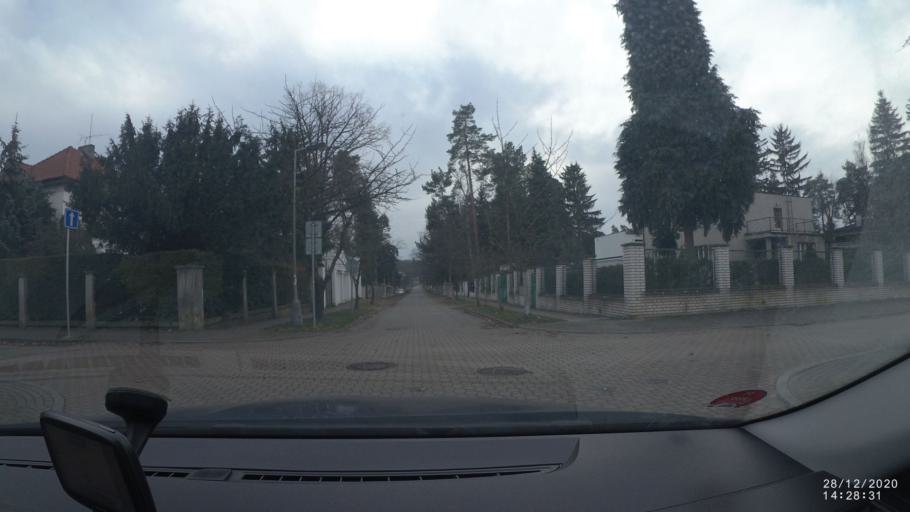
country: CZ
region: Central Bohemia
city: Sestajovice
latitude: 50.0905
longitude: 14.6648
